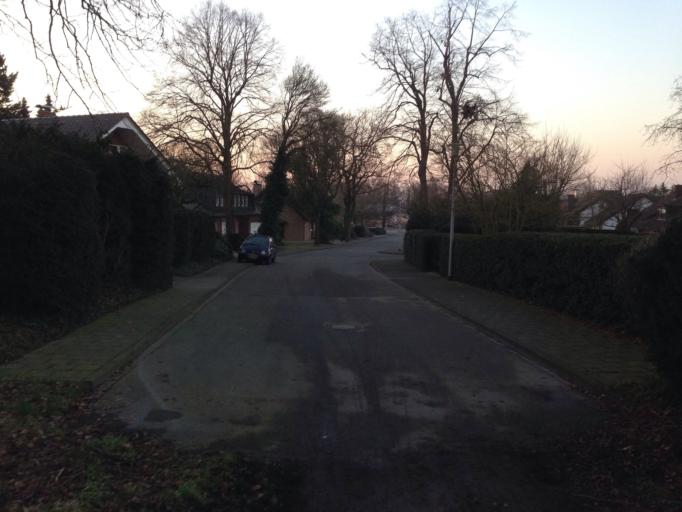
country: DE
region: North Rhine-Westphalia
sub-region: Regierungsbezirk Munster
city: Greven
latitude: 52.0184
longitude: 7.5620
